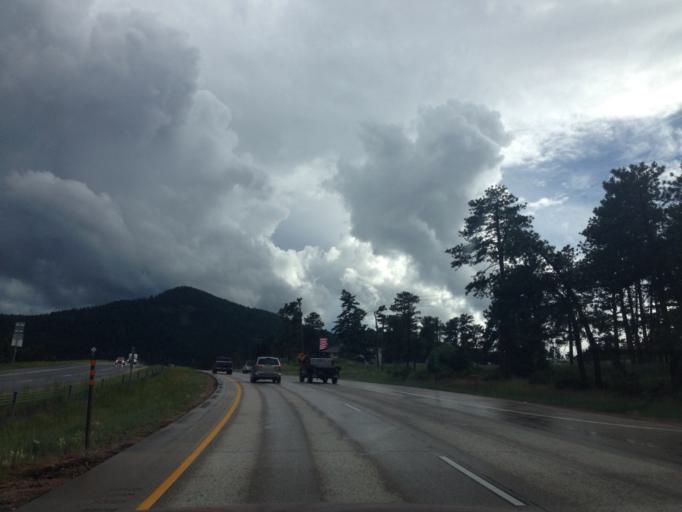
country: US
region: Colorado
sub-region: Jefferson County
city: Indian Hills
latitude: 39.6168
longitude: -105.2303
